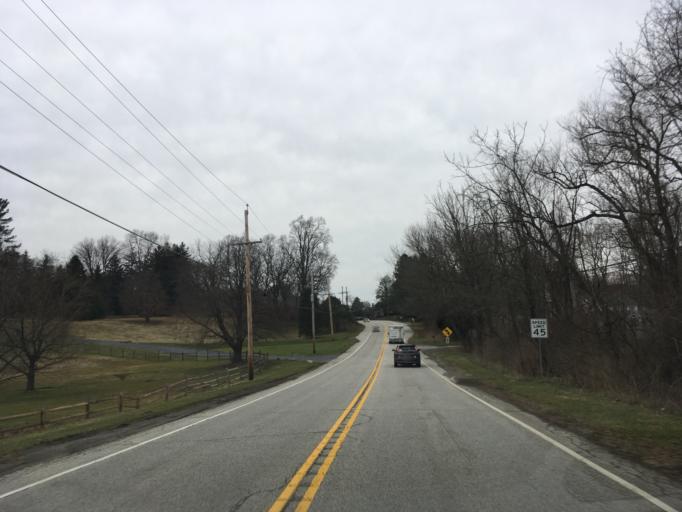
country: US
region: Delaware
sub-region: New Castle County
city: Greenville
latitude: 39.8413
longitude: -75.6302
